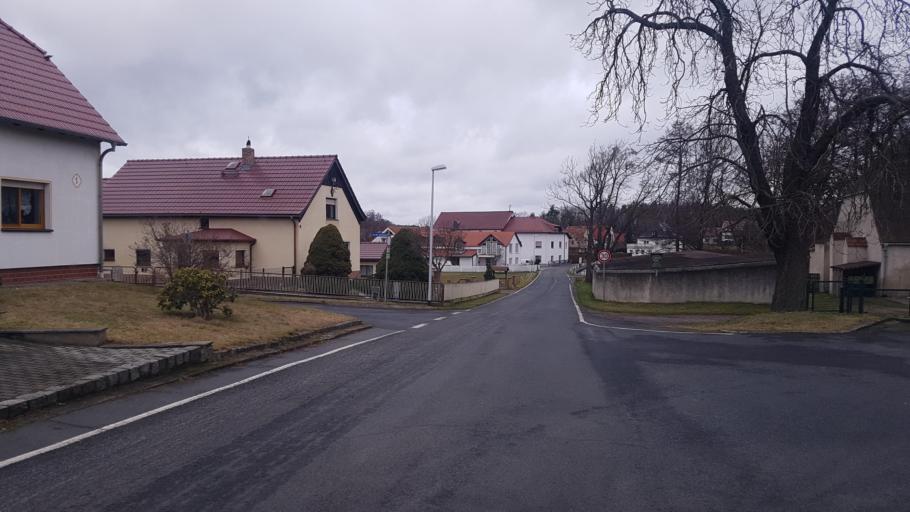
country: DE
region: Brandenburg
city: Kroppen
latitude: 51.3585
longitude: 13.7876
